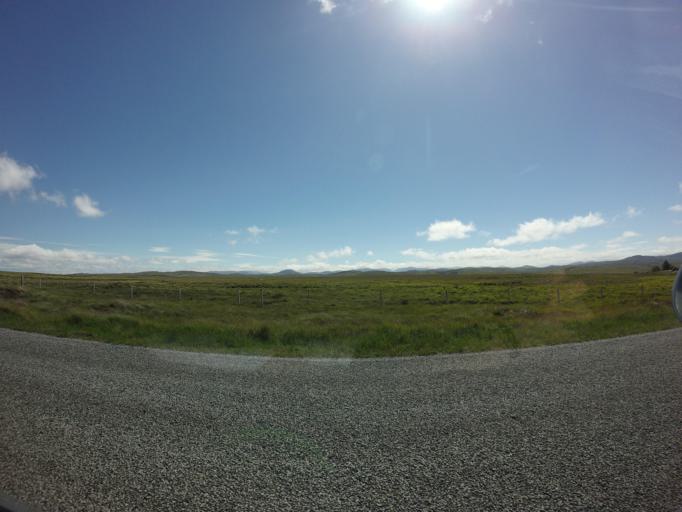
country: GB
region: Scotland
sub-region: Eilean Siar
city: Harris
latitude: 58.1879
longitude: -6.6950
